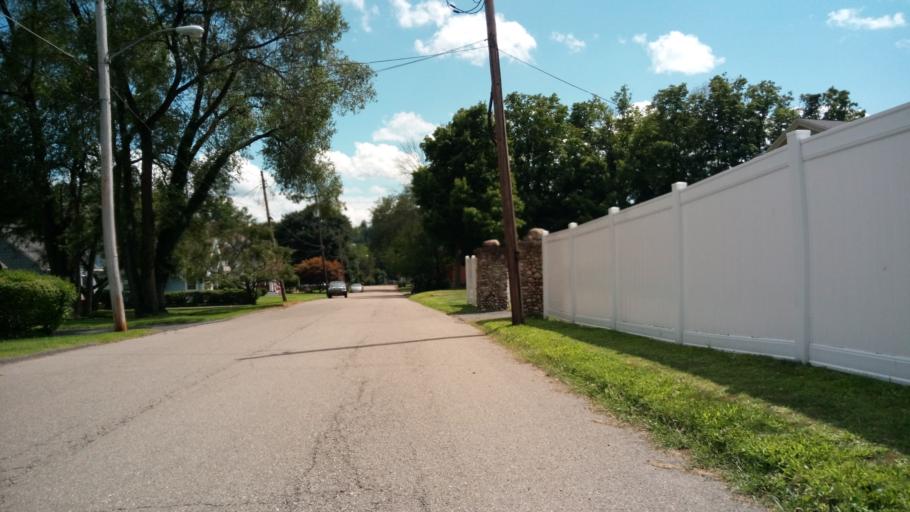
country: US
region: New York
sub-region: Chemung County
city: West Elmira
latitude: 42.0820
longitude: -76.8333
